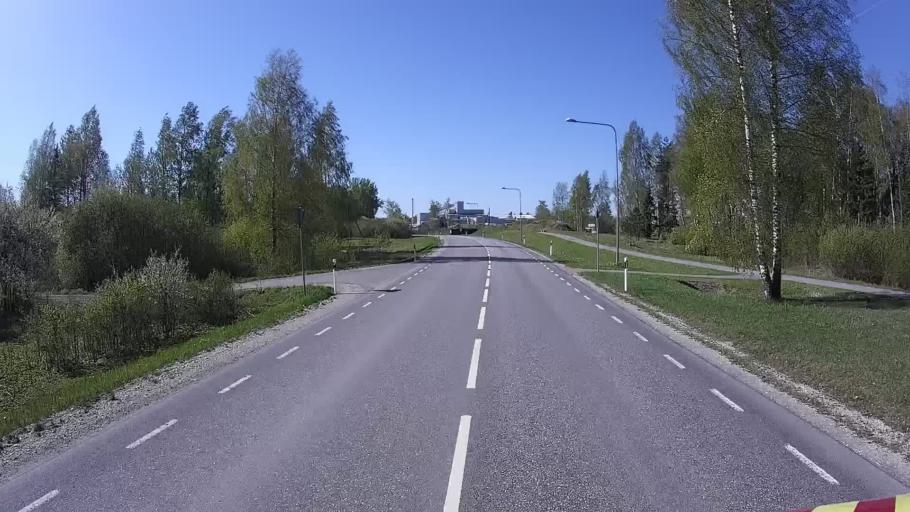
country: EE
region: Raplamaa
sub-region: Jaervakandi vald
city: Jarvakandi
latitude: 58.7836
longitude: 24.8184
